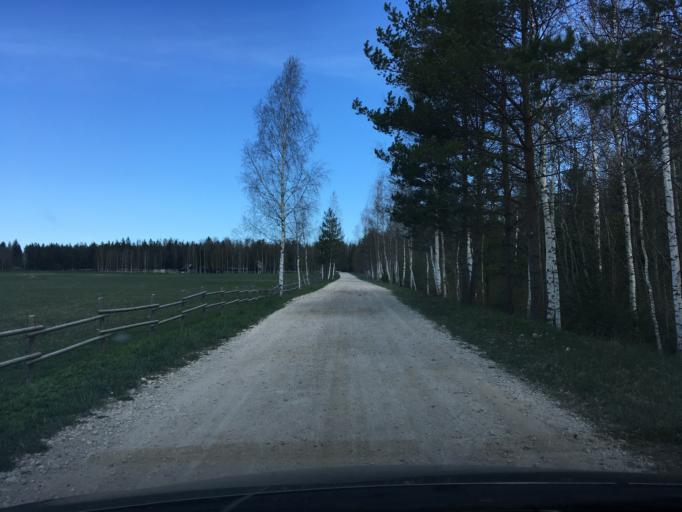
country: EE
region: Harju
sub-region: Raasiku vald
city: Raasiku
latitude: 59.2082
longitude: 25.1723
